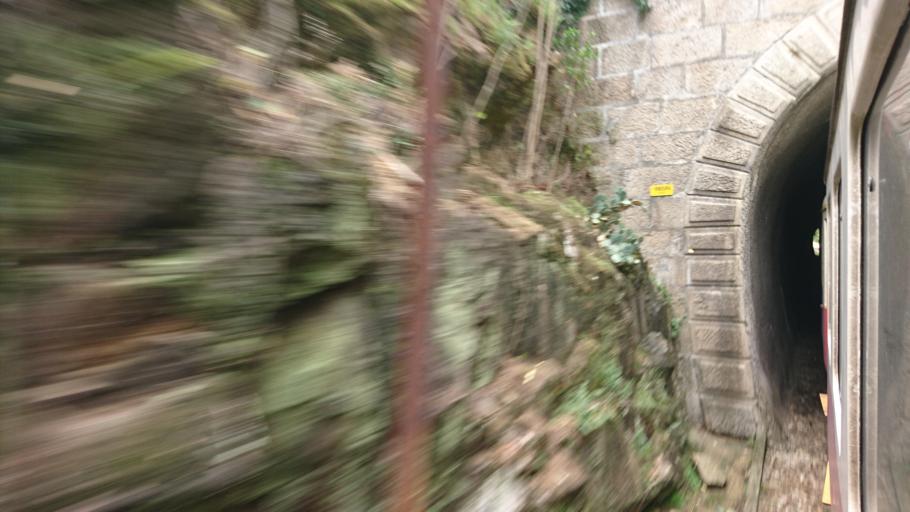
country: PT
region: Viseu
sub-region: Resende
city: Resende
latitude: 41.1240
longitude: -7.9455
